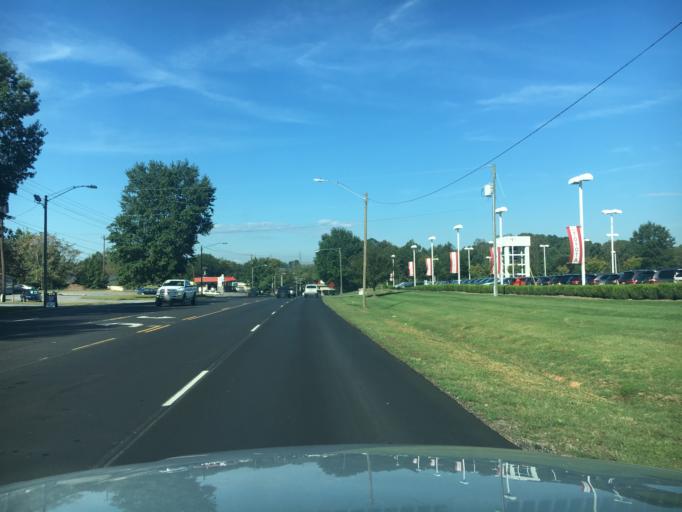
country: US
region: North Carolina
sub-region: Catawba County
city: Hickory
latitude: 35.7117
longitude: -81.3257
